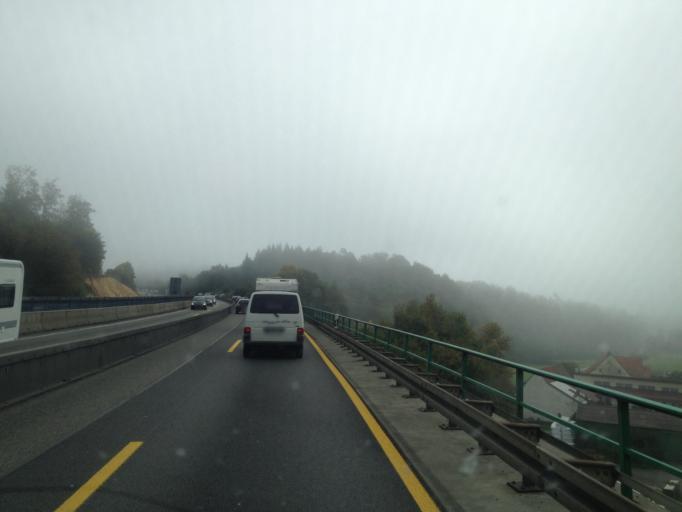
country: DE
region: Baden-Wuerttemberg
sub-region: Freiburg Region
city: Immendingen
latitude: 47.8929
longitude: 8.7112
